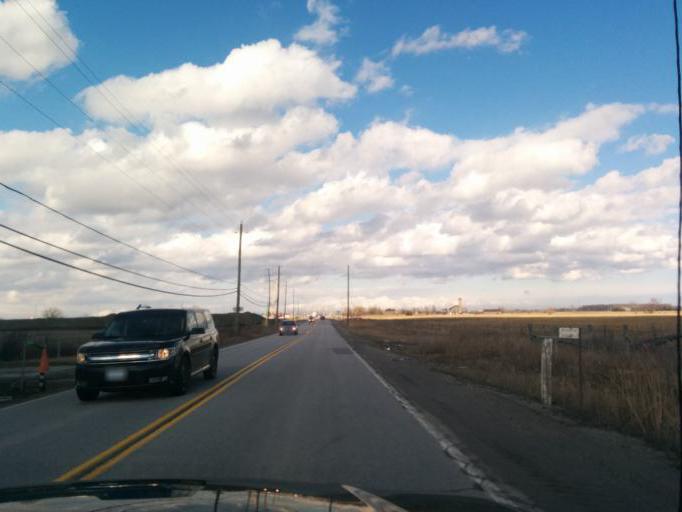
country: CA
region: Ontario
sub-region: Halton
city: Milton
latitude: 43.5078
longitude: -79.8118
